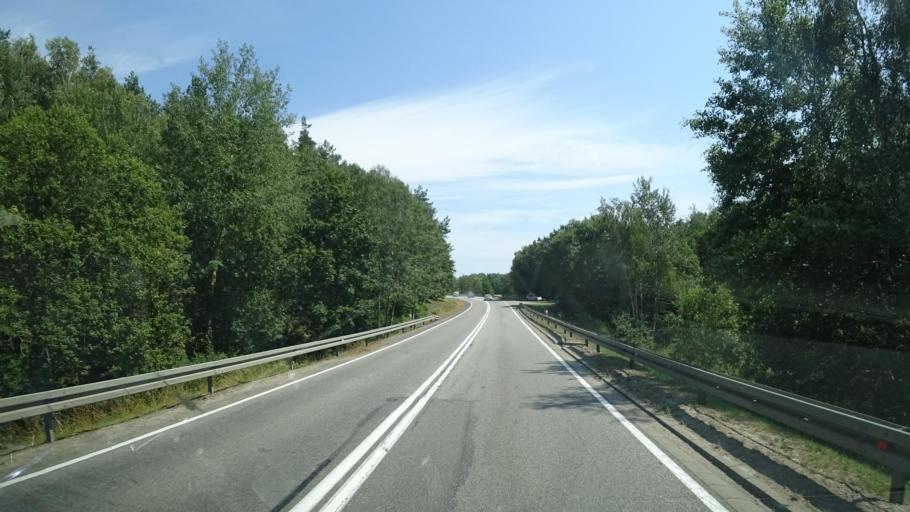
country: PL
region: Pomeranian Voivodeship
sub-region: Powiat koscierski
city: Grabowo Koscierskie
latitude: 54.2228
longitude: 18.1457
